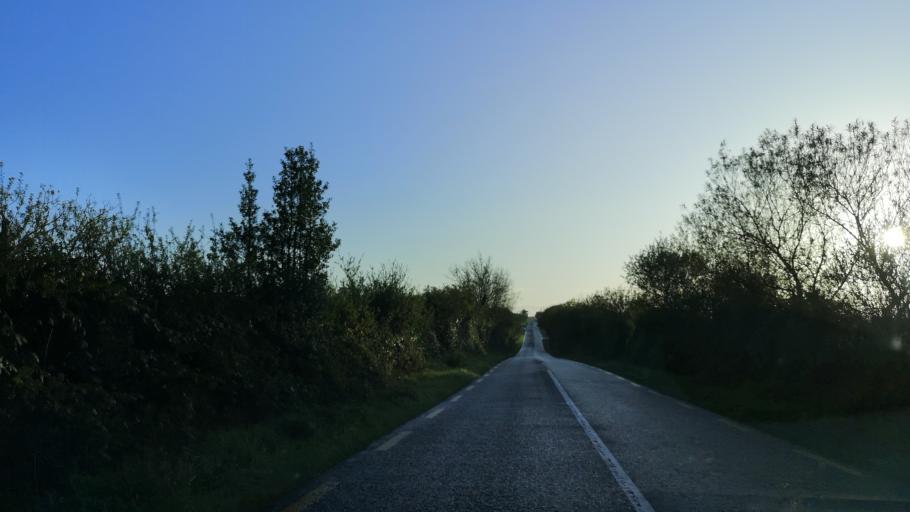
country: IE
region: Connaught
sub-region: Roscommon
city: Castlerea
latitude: 53.7486
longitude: -8.5328
